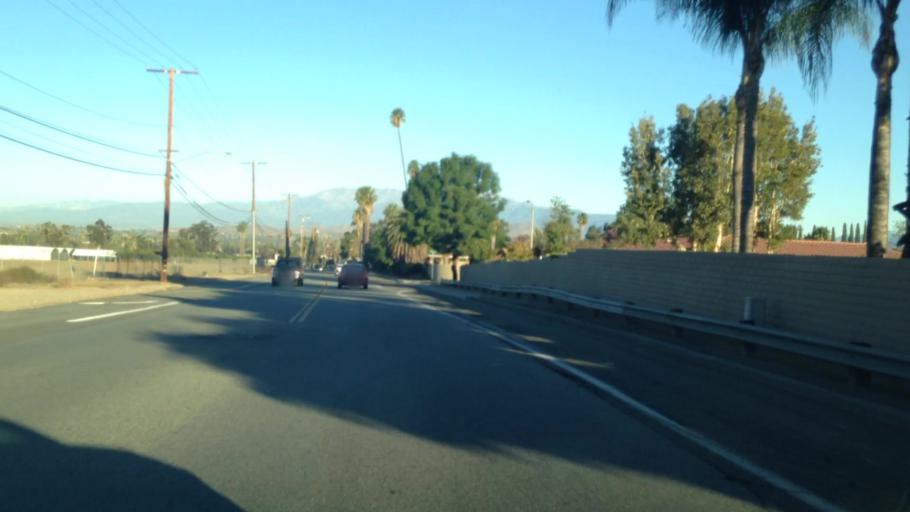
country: US
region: California
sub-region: Riverside County
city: Riverside
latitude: 33.9235
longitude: -117.3839
